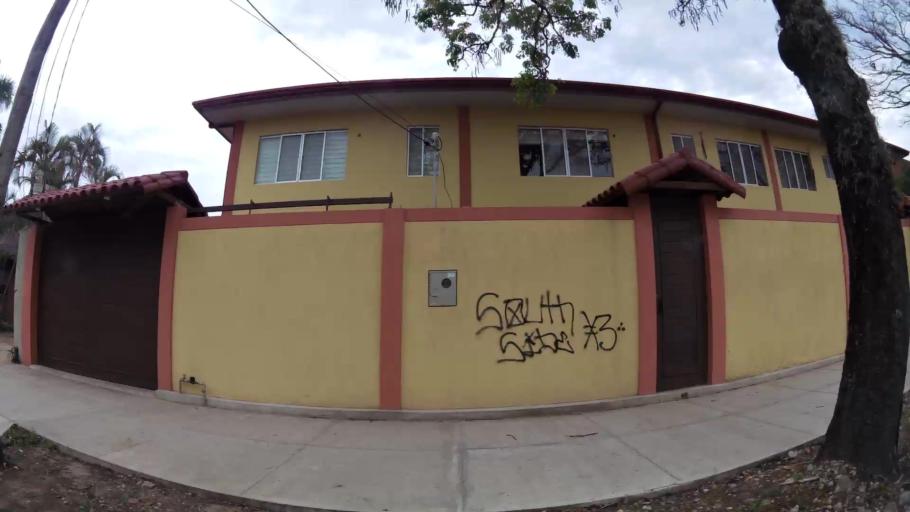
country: BO
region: Santa Cruz
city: Santa Cruz de la Sierra
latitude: -17.7741
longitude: -63.1705
